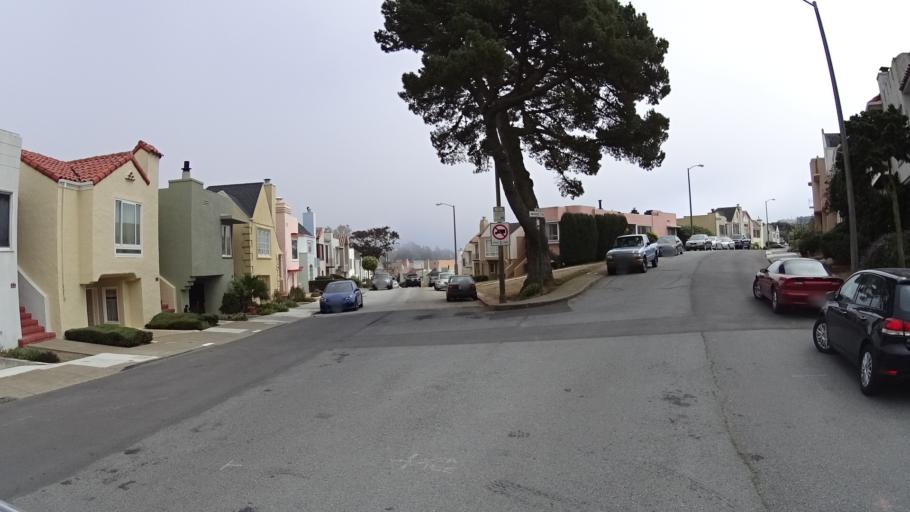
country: US
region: California
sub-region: San Mateo County
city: Daly City
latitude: 37.7419
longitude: -122.4492
